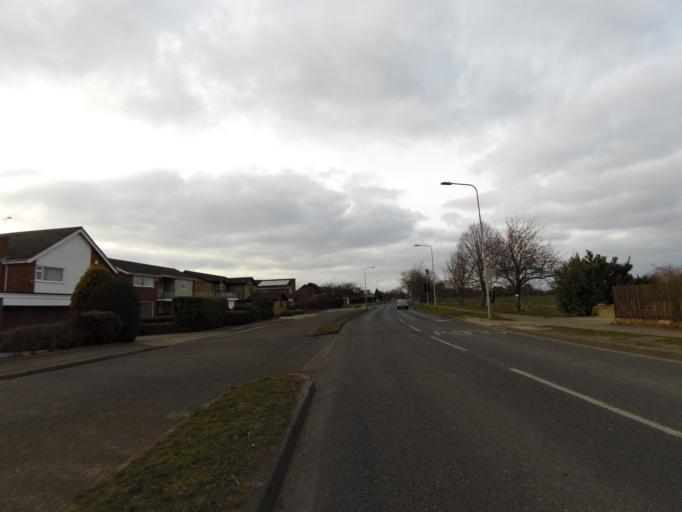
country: GB
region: England
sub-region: Suffolk
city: Ipswich
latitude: 52.0787
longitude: 1.1507
